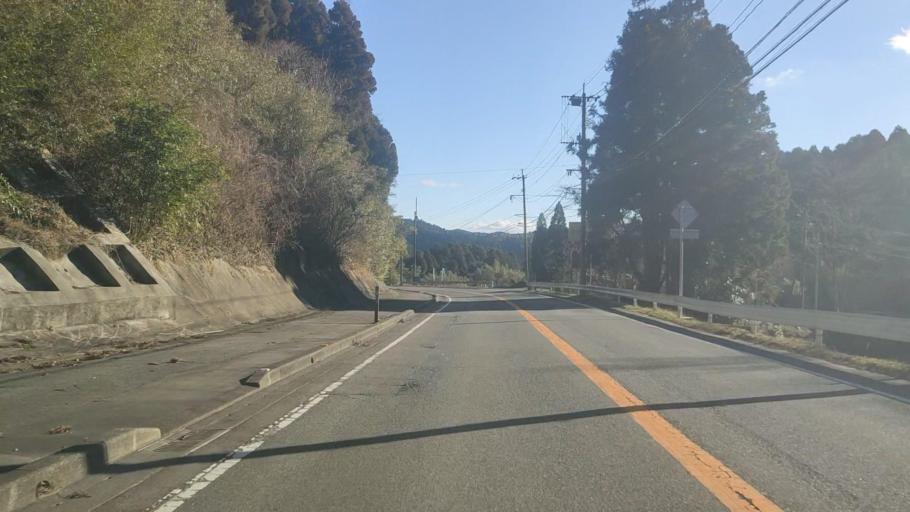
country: JP
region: Fukuoka
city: Maebaru-chuo
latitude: 33.4573
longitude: 130.2740
